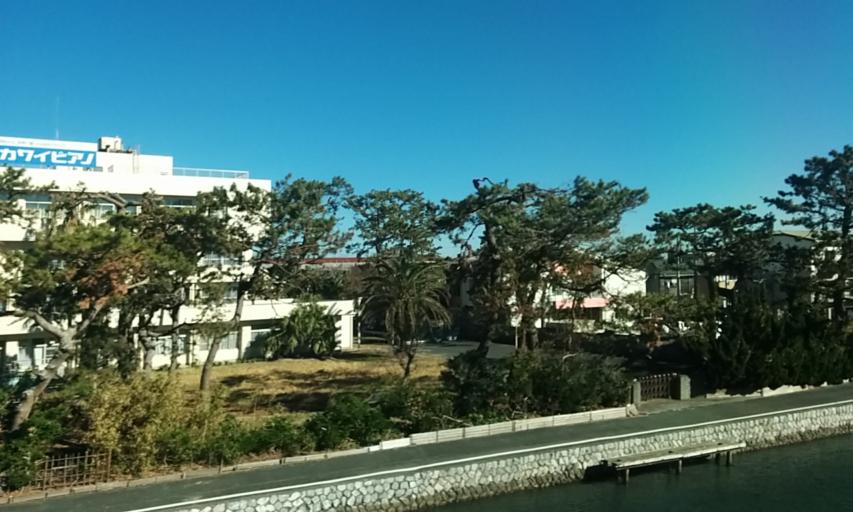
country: JP
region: Shizuoka
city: Kosai-shi
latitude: 34.6914
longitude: 137.6008
